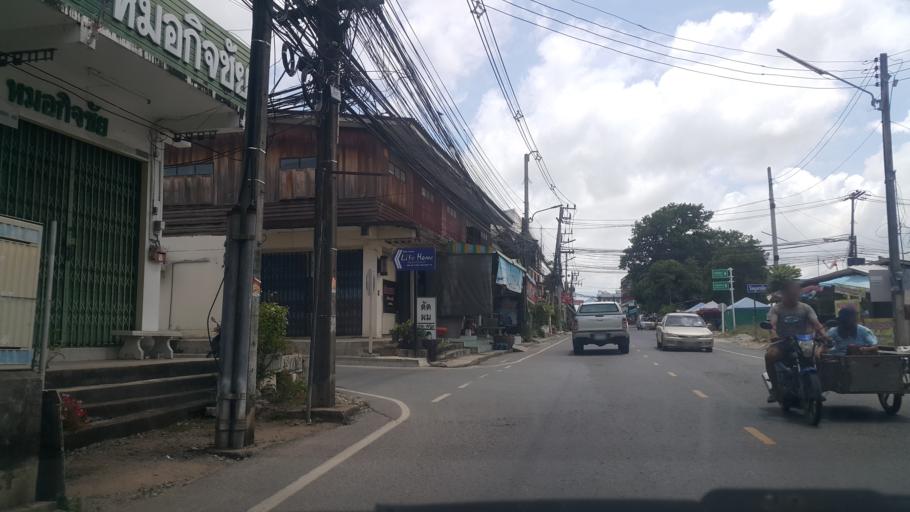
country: TH
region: Rayong
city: Ban Chang
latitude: 12.7273
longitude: 101.0528
